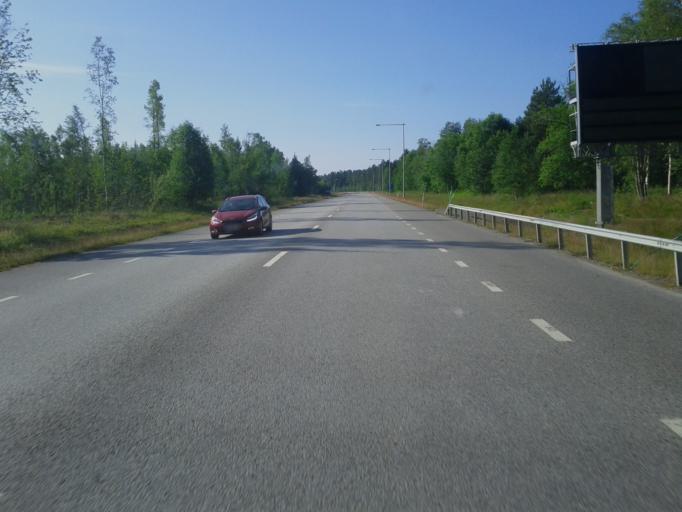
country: SE
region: Vaesterbotten
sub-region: Umea Kommun
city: Umea
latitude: 63.7883
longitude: 20.3011
